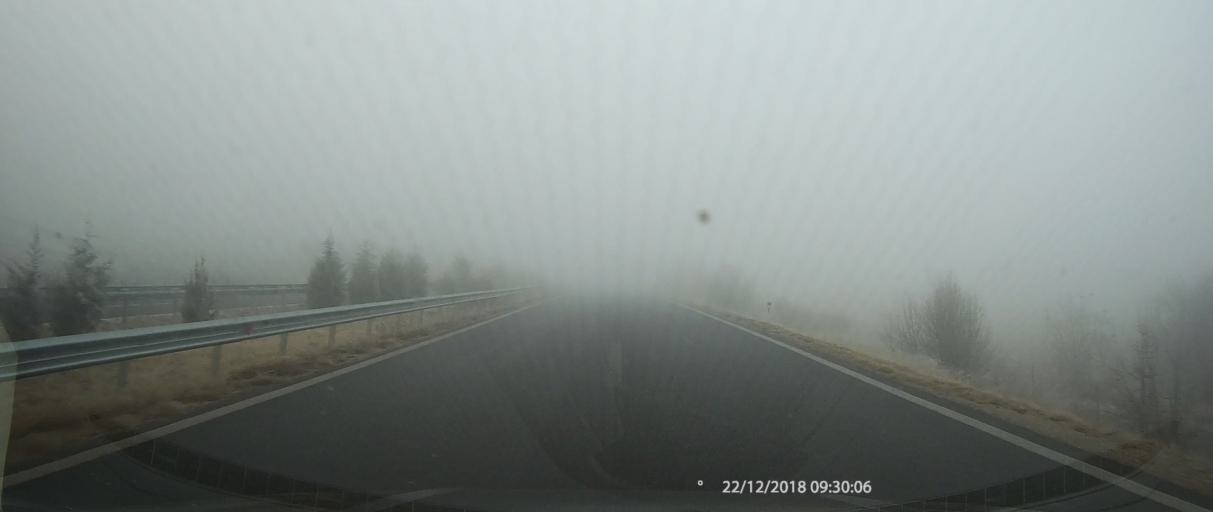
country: MK
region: Kumanovo
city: Romanovce
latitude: 42.0965
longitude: 21.7033
